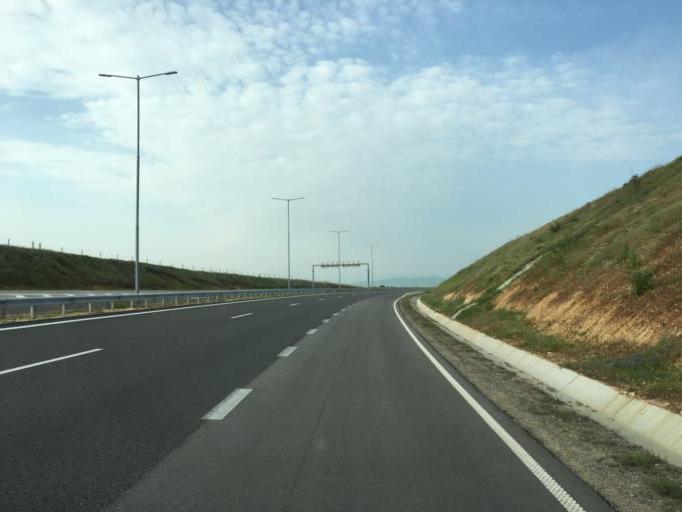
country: BG
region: Kyustendil
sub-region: Obshtina Kocherinovo
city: Kocherinovo
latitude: 42.0522
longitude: 23.0475
